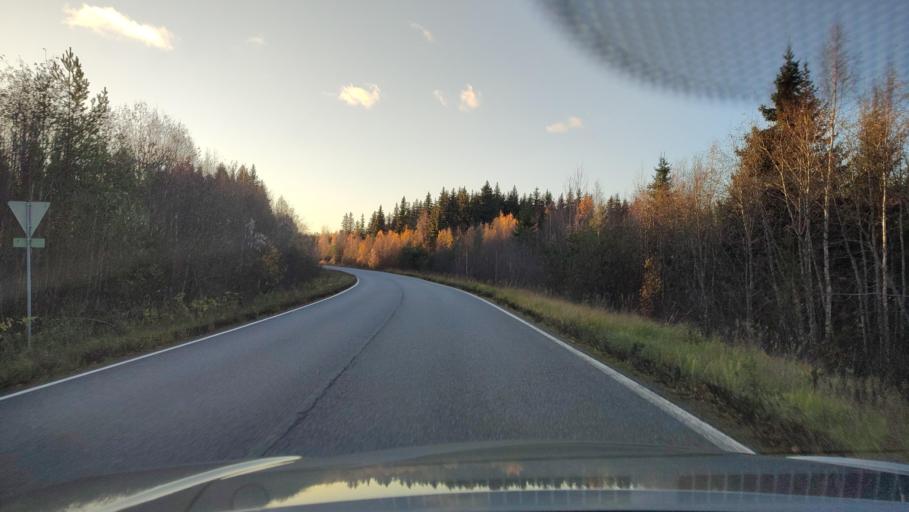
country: FI
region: Ostrobothnia
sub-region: Sydosterbotten
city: Kristinestad
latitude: 62.2961
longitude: 21.3787
